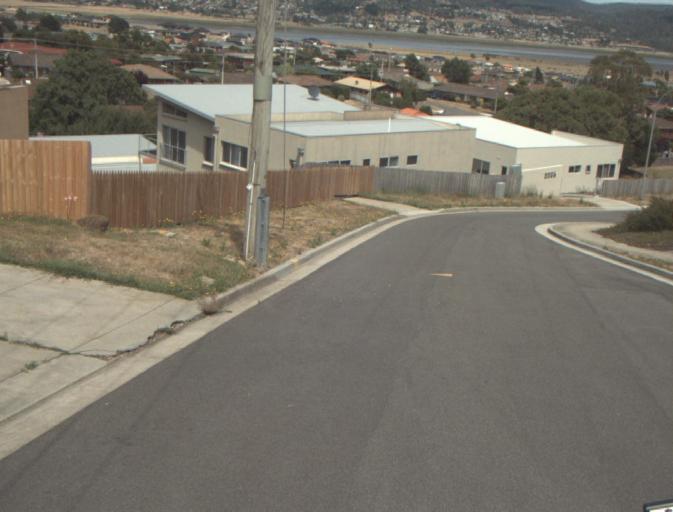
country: AU
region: Tasmania
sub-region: Launceston
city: Mayfield
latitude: -41.3815
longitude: 147.1187
